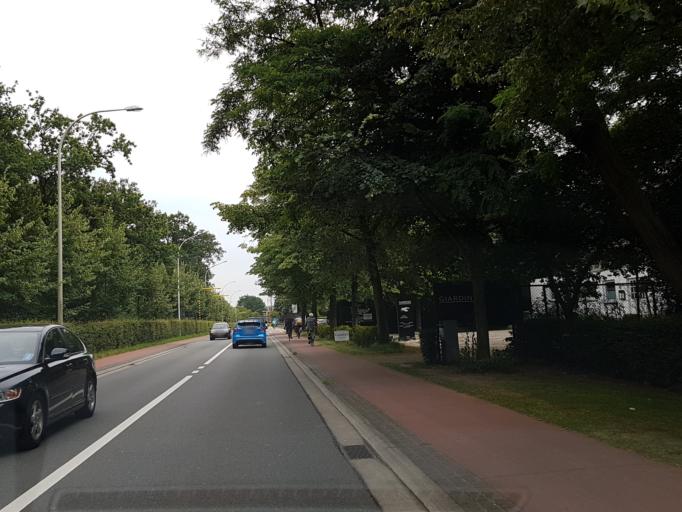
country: BE
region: Flanders
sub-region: Provincie Antwerpen
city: Schoten
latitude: 51.2581
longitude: 4.4852
